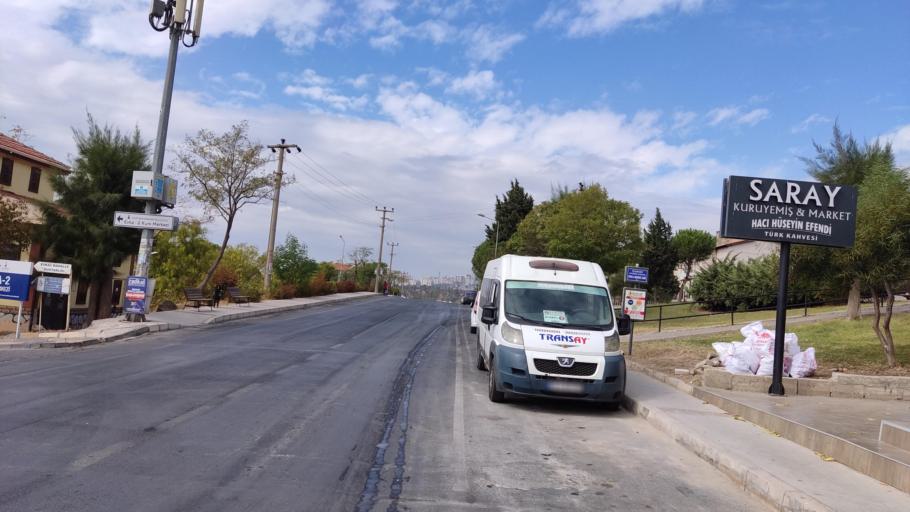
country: TR
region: Izmir
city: Karsiyaka
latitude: 38.5001
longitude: 27.0869
